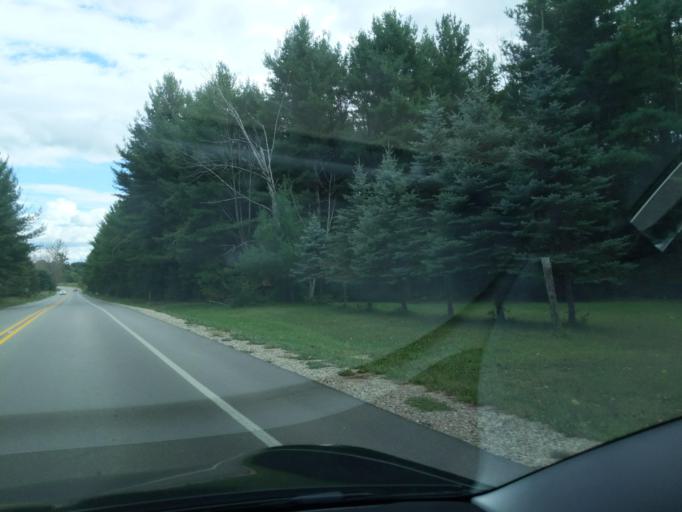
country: US
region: Michigan
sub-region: Kalkaska County
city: Rapid City
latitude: 44.8959
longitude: -85.2765
